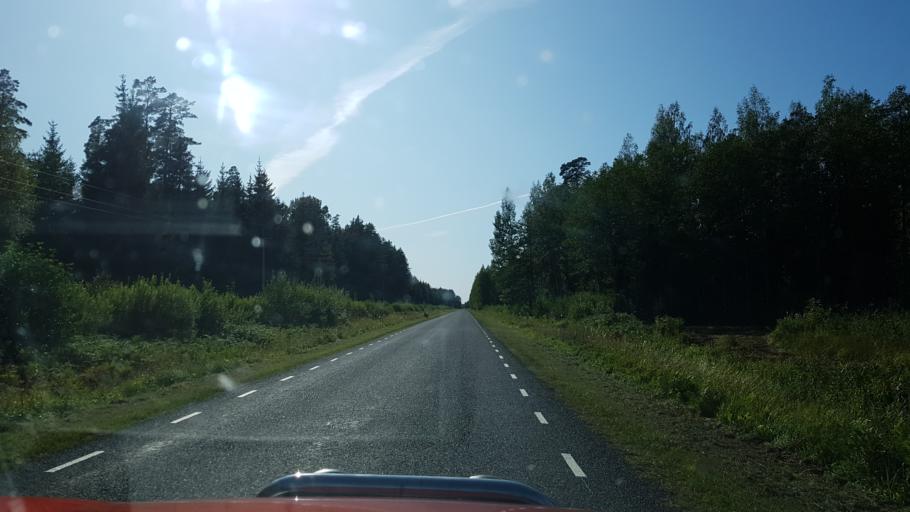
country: EE
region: Paernumaa
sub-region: Paikuse vald
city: Paikuse
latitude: 58.0831
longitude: 24.5747
